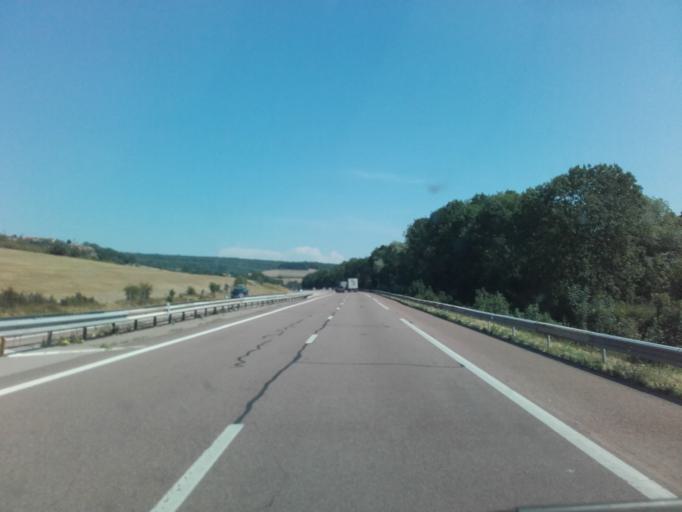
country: FR
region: Bourgogne
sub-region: Departement de la Cote-d'Or
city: Pouilly-en-Auxois
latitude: 47.2013
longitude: 4.6497
